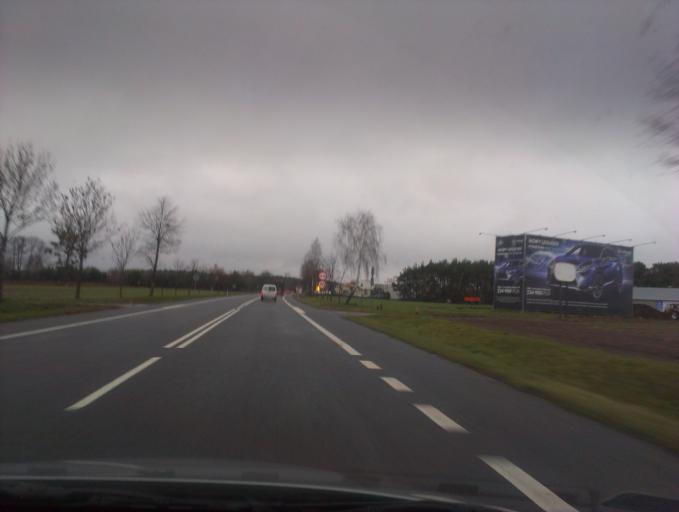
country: PL
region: Greater Poland Voivodeship
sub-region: Powiat chodzieski
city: Budzyn
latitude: 52.8972
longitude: 16.9699
